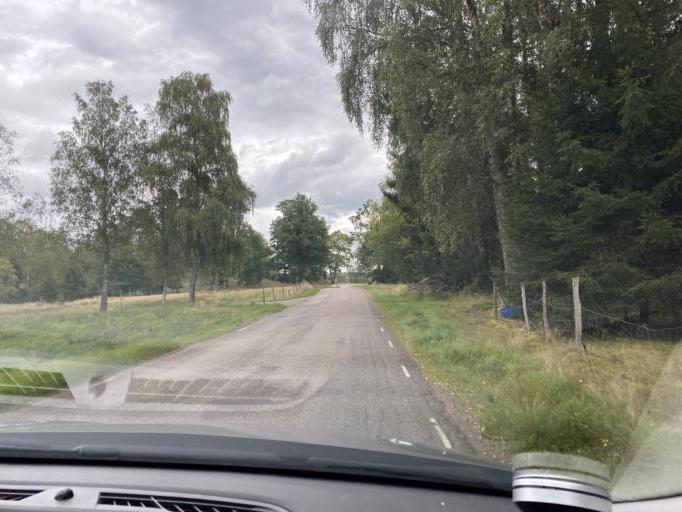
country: SE
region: Kronoberg
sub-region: Markaryds Kommun
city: Markaryd
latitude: 56.4881
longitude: 13.5454
